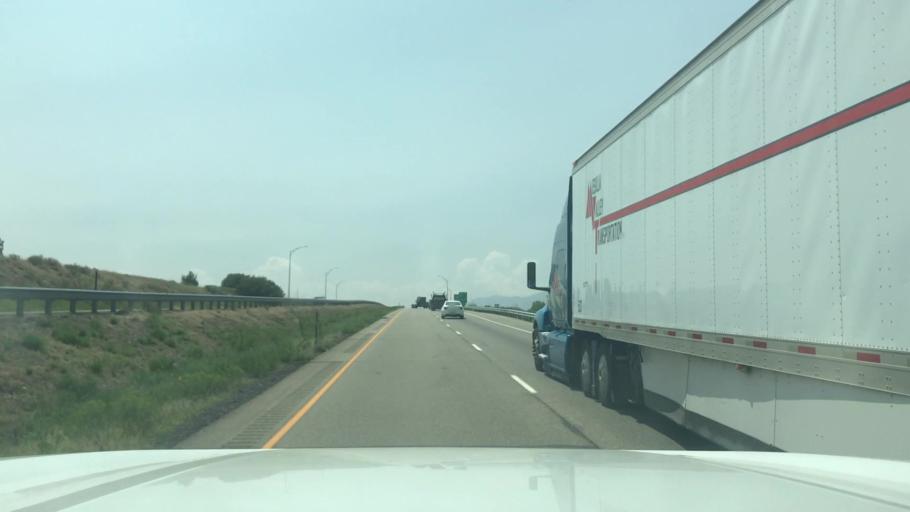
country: US
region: Colorado
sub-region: Pueblo County
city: Colorado City
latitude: 37.9673
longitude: -104.7898
